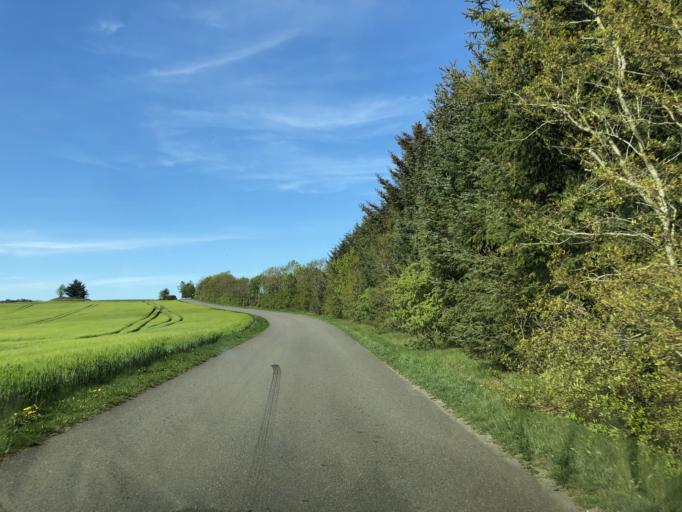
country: DK
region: Central Jutland
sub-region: Ringkobing-Skjern Kommune
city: Videbaek
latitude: 56.2001
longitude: 8.5127
